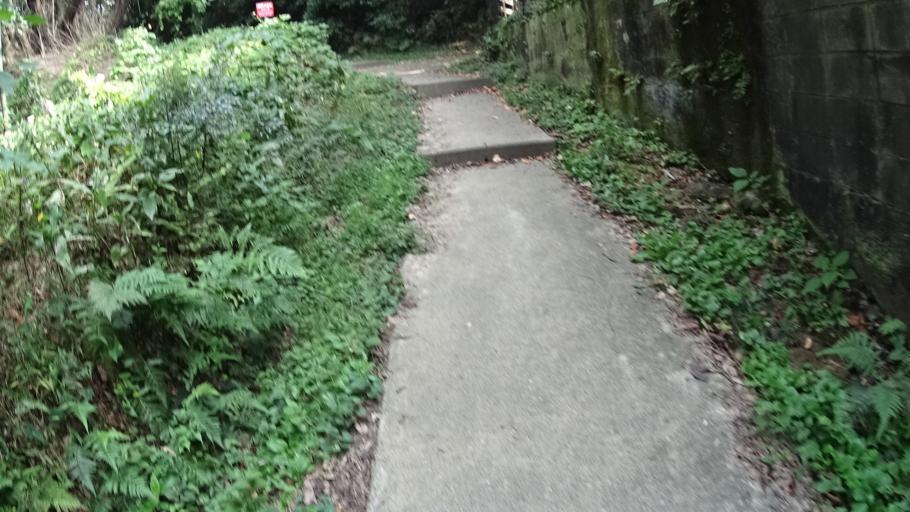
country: JP
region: Kanagawa
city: Zushi
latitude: 35.3011
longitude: 139.6026
